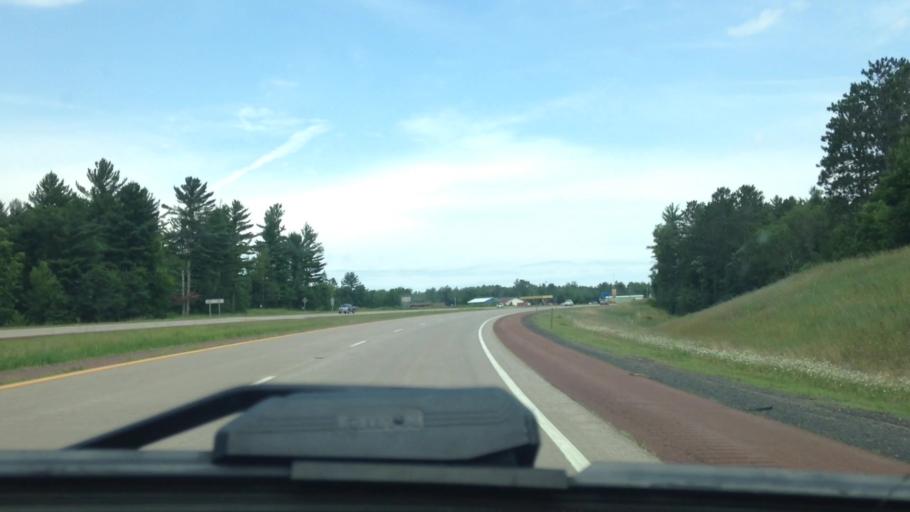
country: US
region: Wisconsin
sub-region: Douglas County
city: Lake Nebagamon
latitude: 46.3470
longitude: -91.8354
